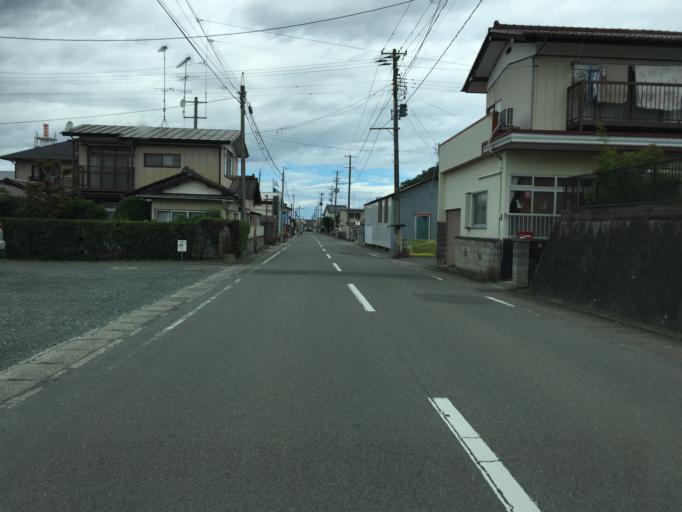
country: JP
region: Fukushima
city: Namie
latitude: 37.6292
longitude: 140.9625
